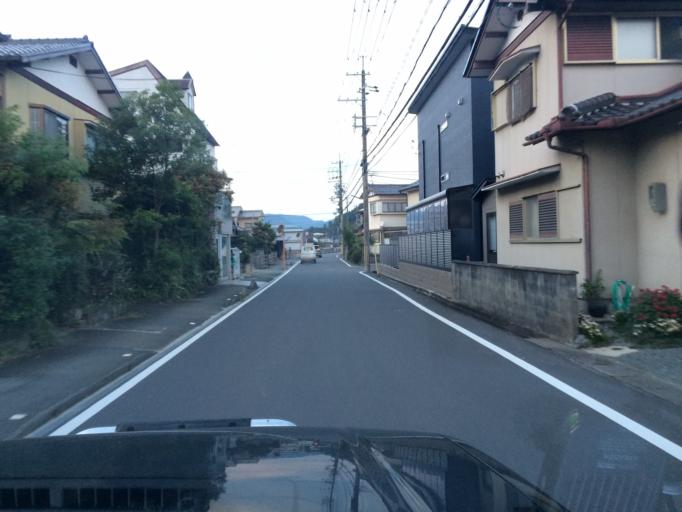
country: JP
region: Kyoto
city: Kameoka
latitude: 35.0968
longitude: 135.4747
